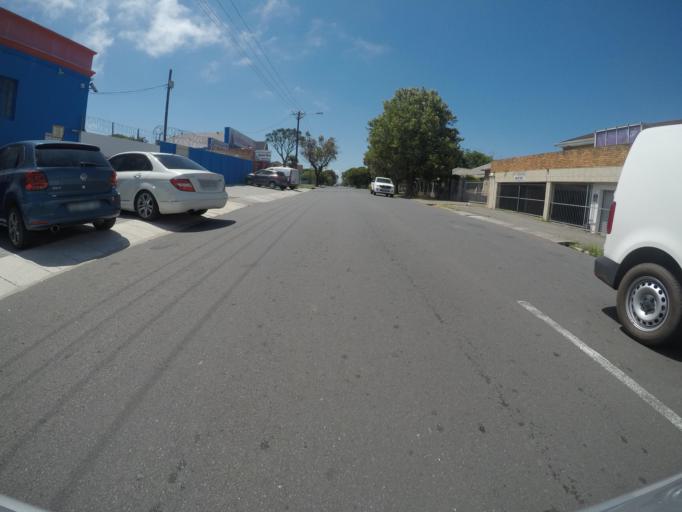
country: ZA
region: Eastern Cape
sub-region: Buffalo City Metropolitan Municipality
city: East London
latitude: -32.9786
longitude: 27.9024
